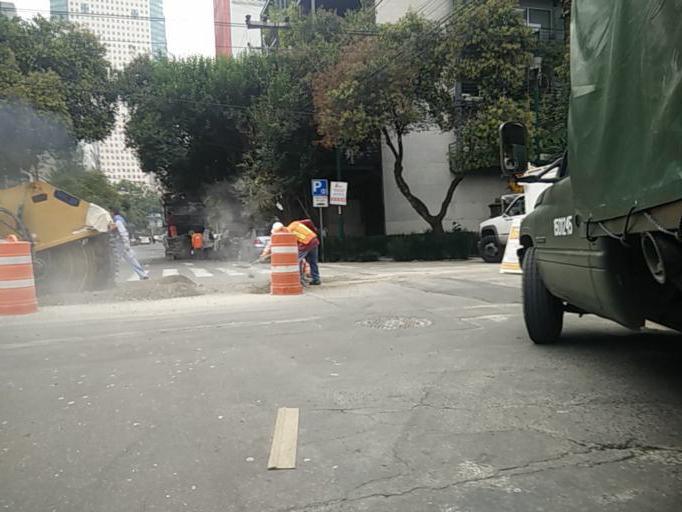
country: MX
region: Mexico City
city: Miguel Hidalgo
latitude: 19.4276
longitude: -99.1769
